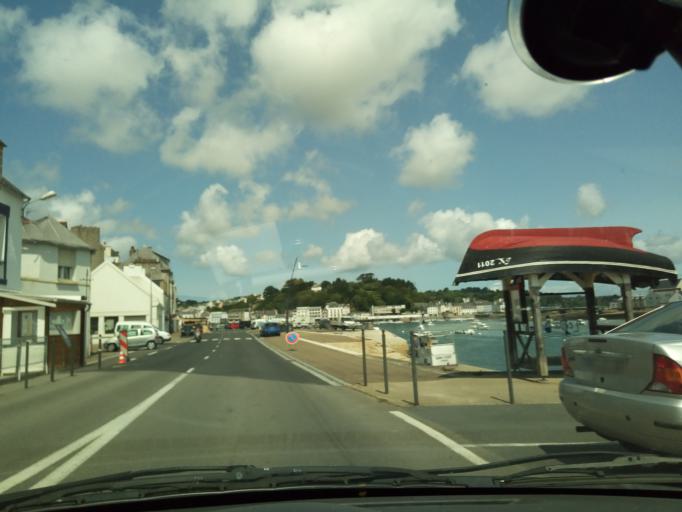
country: FR
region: Brittany
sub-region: Departement du Finistere
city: Audierne
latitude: 48.0193
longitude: -4.5352
